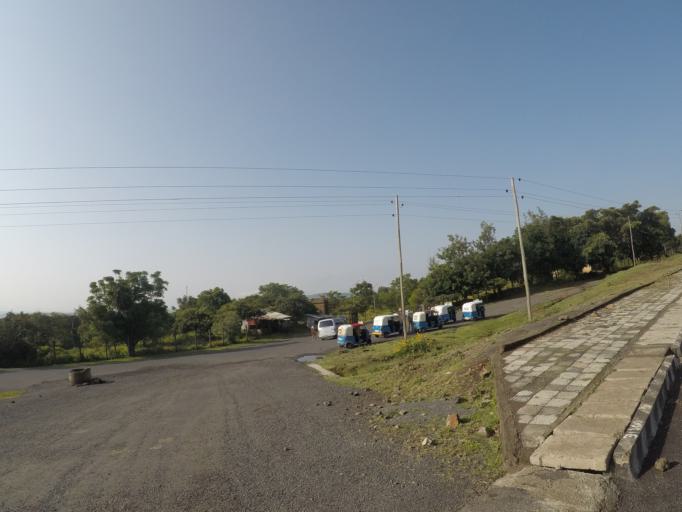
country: ET
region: Amhara
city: Gondar
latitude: 12.5210
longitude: 37.4300
